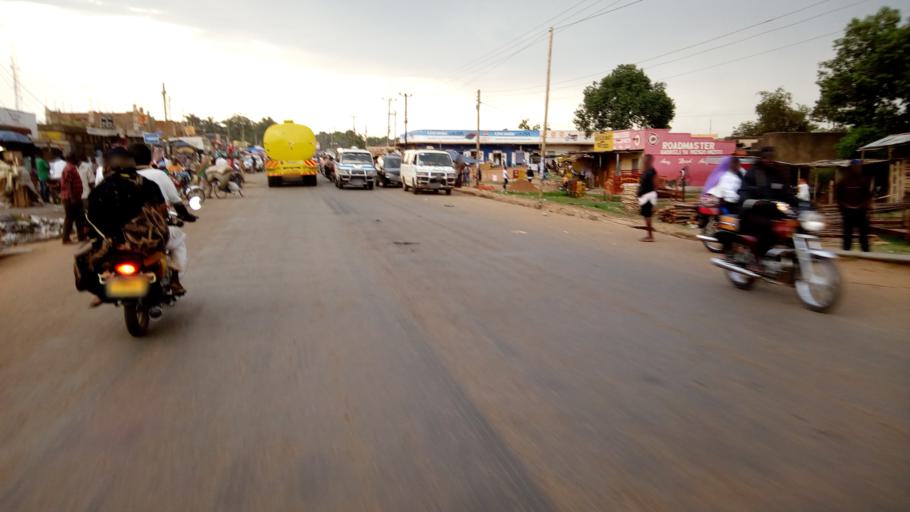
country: UG
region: Eastern Region
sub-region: Mbale District
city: Mbale
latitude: 1.0940
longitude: 34.1763
